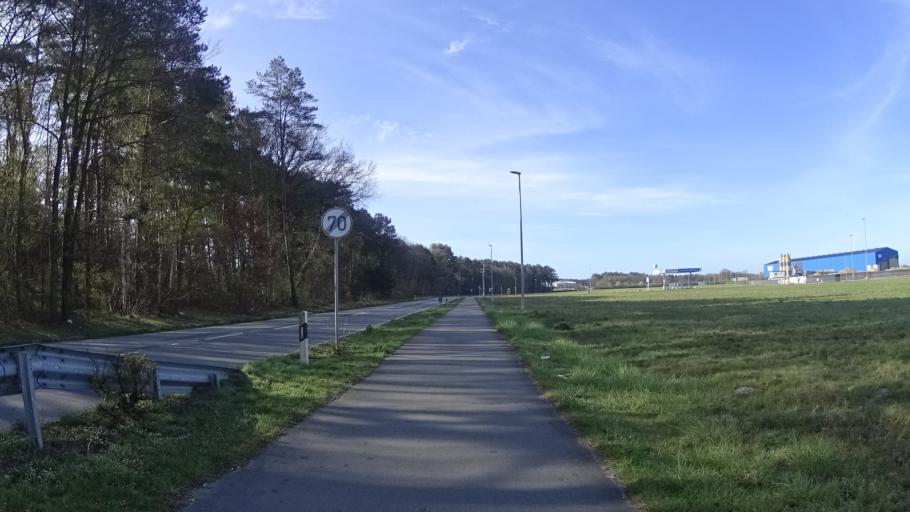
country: DE
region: Lower Saxony
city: Haren
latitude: 52.7764
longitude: 7.2773
